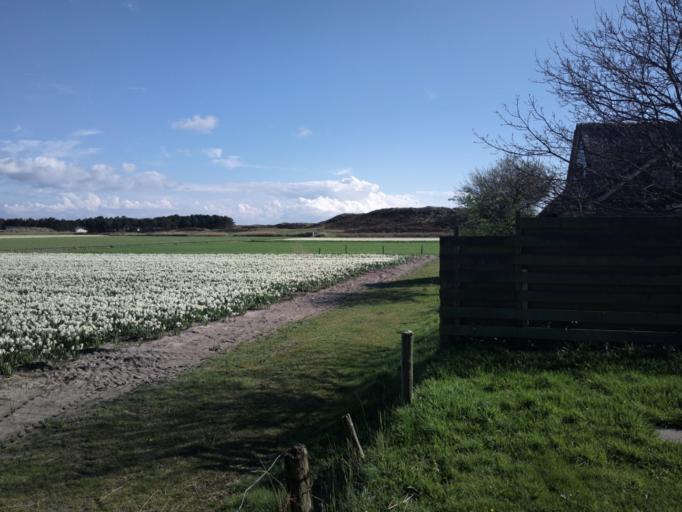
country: NL
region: North Holland
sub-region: Gemeente Den Helder
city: Den Helder
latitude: 53.0234
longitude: 4.7336
